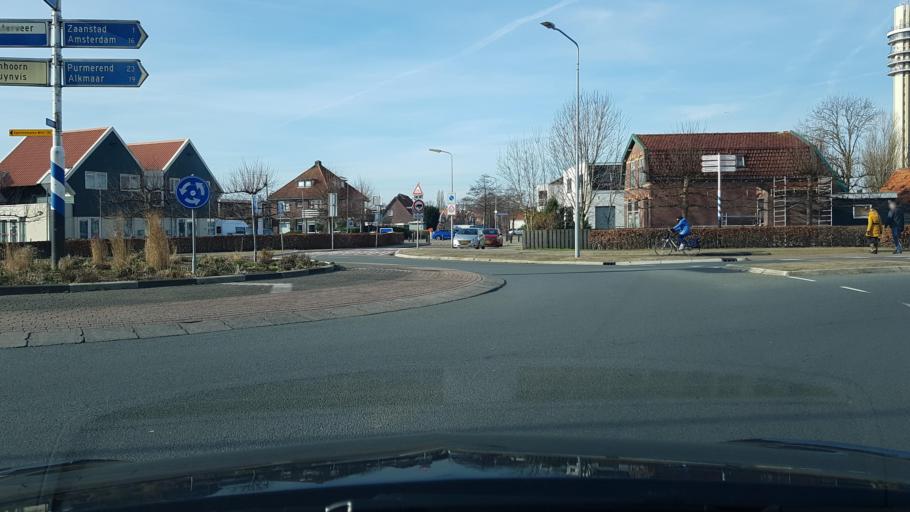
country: NL
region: North Holland
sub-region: Gemeente Zaanstad
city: Zaanstad
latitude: 52.4961
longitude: 4.8022
